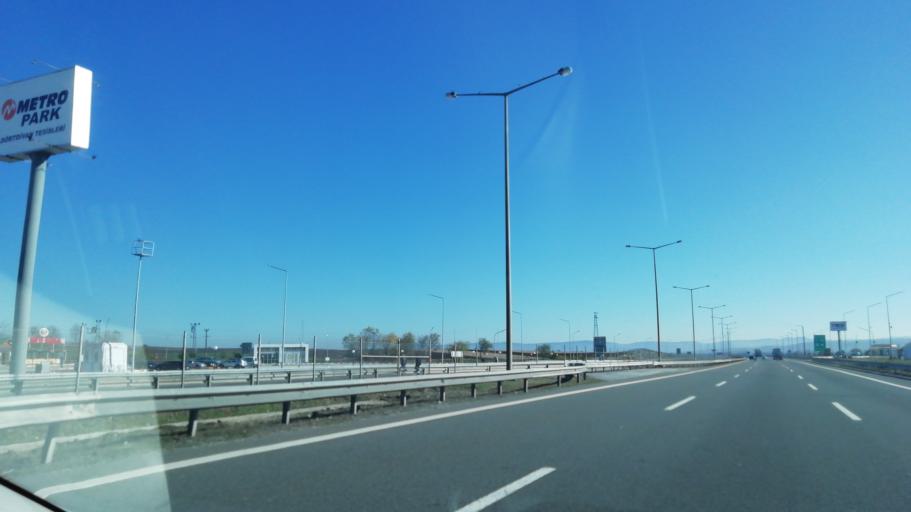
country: TR
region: Bolu
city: Dortdivan
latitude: 40.7502
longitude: 32.0822
